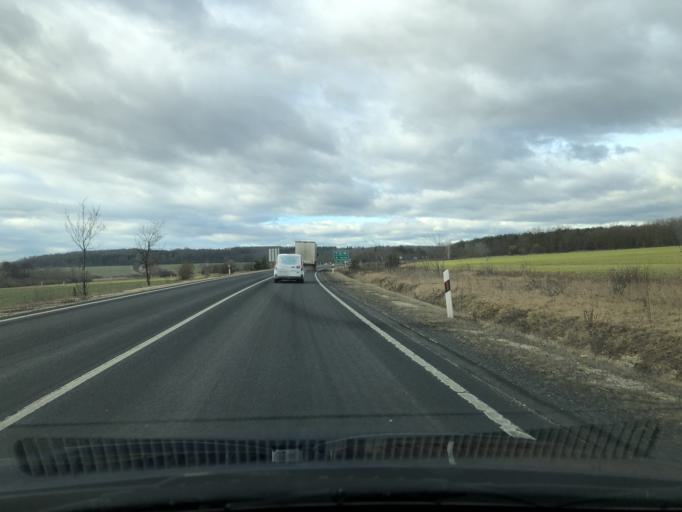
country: AT
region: Burgenland
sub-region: Politischer Bezirk Oberwart
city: Schachendorf
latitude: 47.2461
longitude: 16.4911
